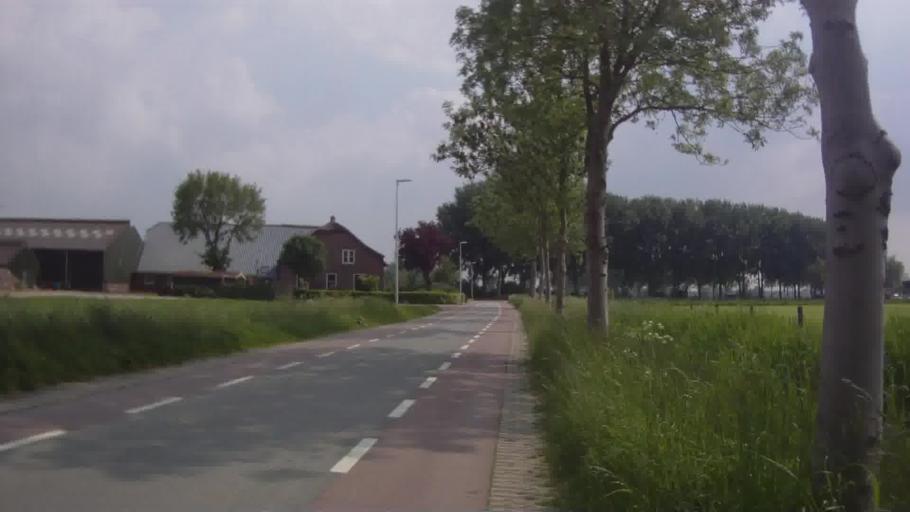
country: NL
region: Utrecht
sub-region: Gemeente Bunnik
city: Bunnik
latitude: 52.0571
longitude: 5.1895
